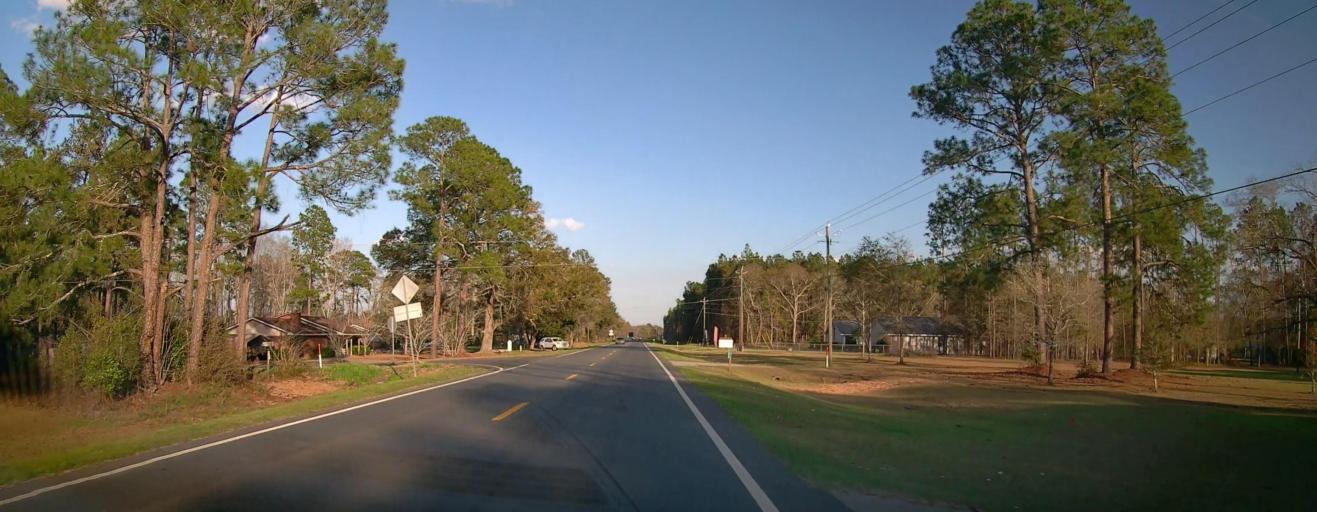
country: US
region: Georgia
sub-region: Evans County
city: Claxton
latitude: 32.1609
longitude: -81.8727
